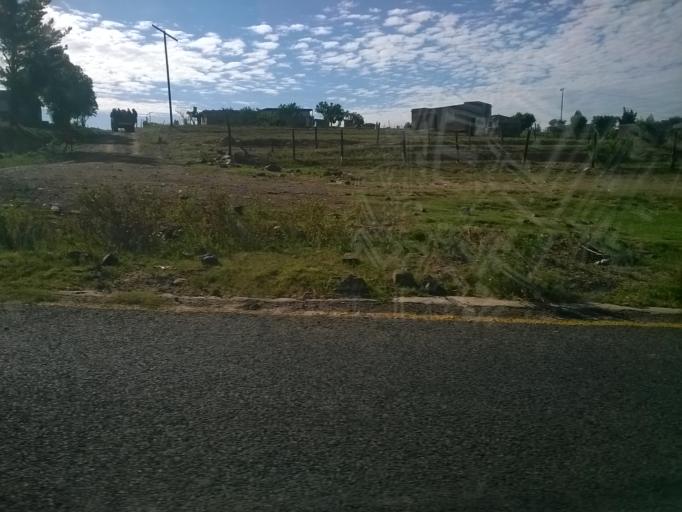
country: LS
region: Berea
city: Teyateyaneng
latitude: -29.1228
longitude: 27.7885
